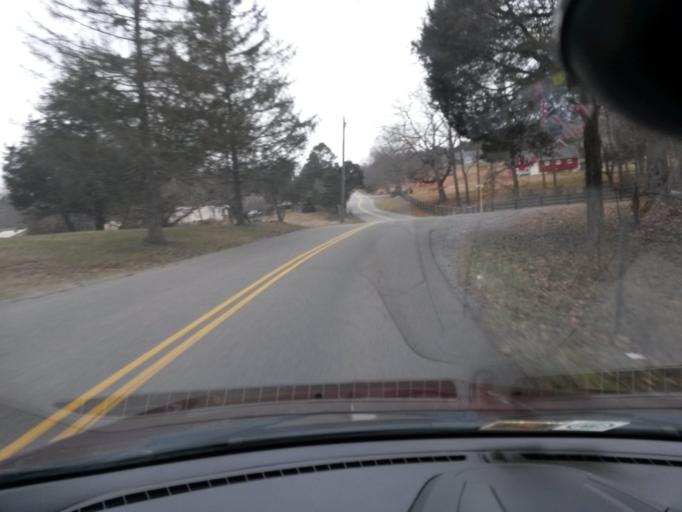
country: US
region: Virginia
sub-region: Rockbridge County
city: East Lexington
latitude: 37.7886
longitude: -79.3726
